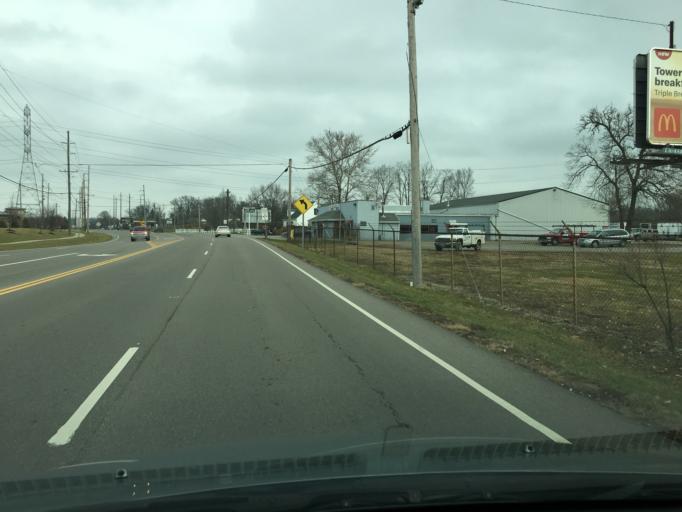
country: US
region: Ohio
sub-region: Butler County
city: Beckett Ridge
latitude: 39.3208
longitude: -84.4112
